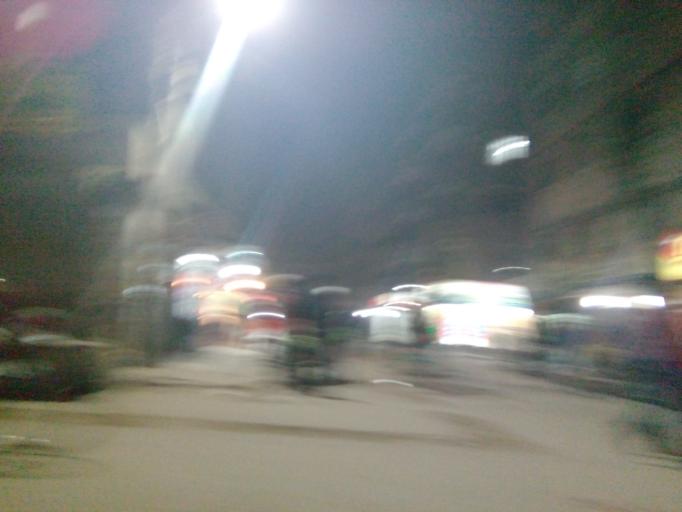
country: BD
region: Dhaka
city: Paltan
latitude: 23.7475
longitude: 90.4285
